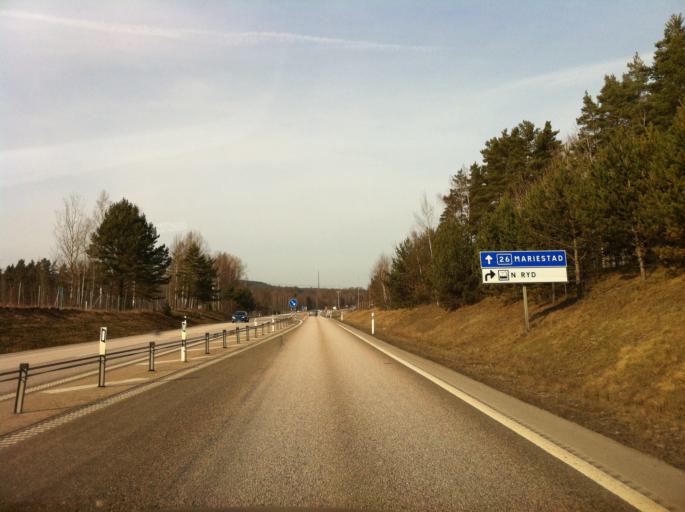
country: SE
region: Vaestra Goetaland
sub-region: Skovde Kommun
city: Stopen
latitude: 58.4420
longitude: 13.8546
